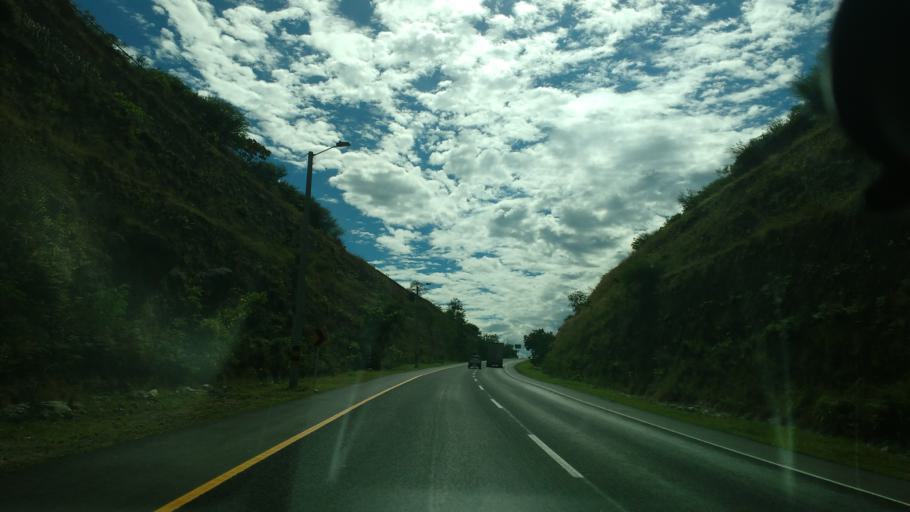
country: CO
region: Tolima
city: Valle de San Juan
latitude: 4.2931
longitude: -75.0404
